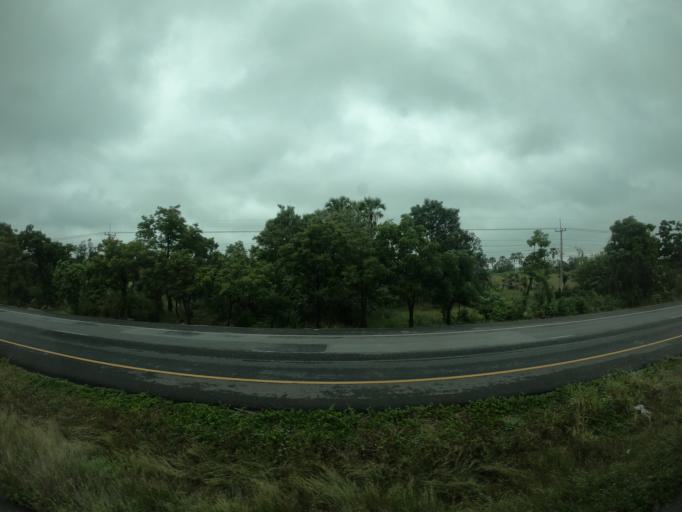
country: TH
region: Nakhon Ratchasima
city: Non Daeng
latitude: 15.4405
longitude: 102.4937
